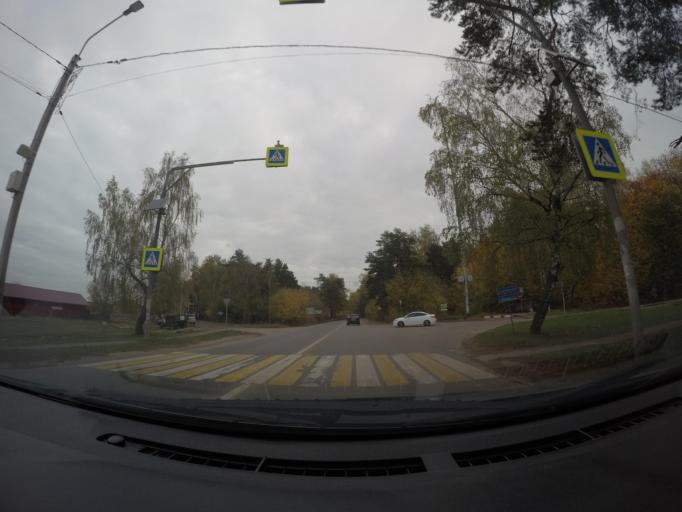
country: RU
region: Moskovskaya
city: Elektrougli
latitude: 55.7693
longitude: 38.2248
